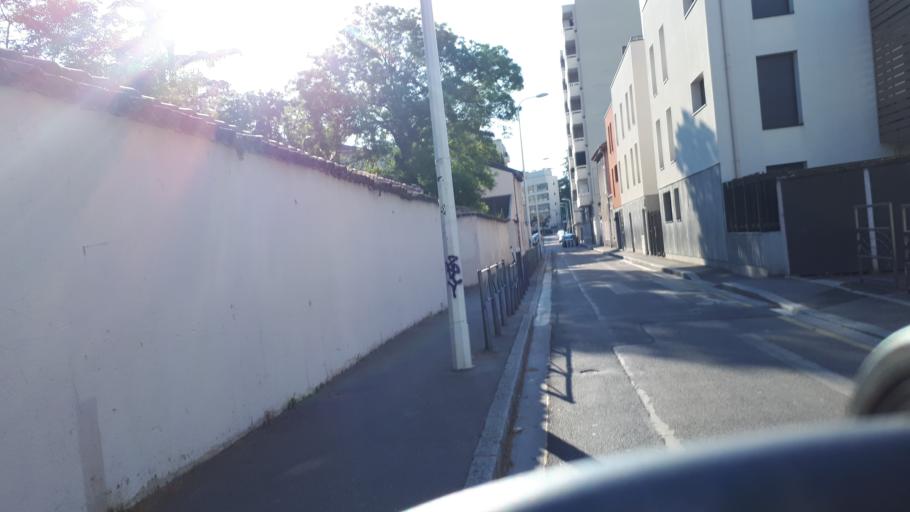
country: FR
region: Rhone-Alpes
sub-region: Departement du Rhone
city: Lyon
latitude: 45.7415
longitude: 4.8729
